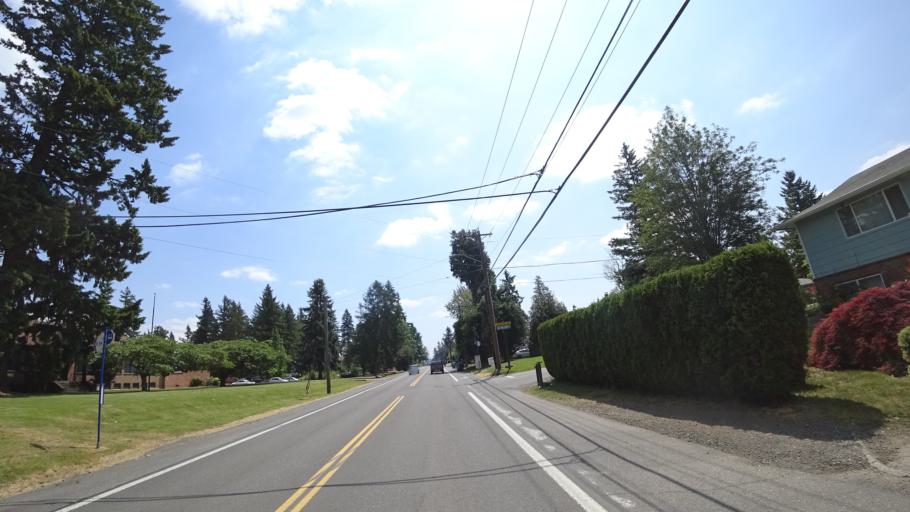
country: US
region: Oregon
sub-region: Multnomah County
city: Fairview
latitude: 45.5301
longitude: -122.4962
